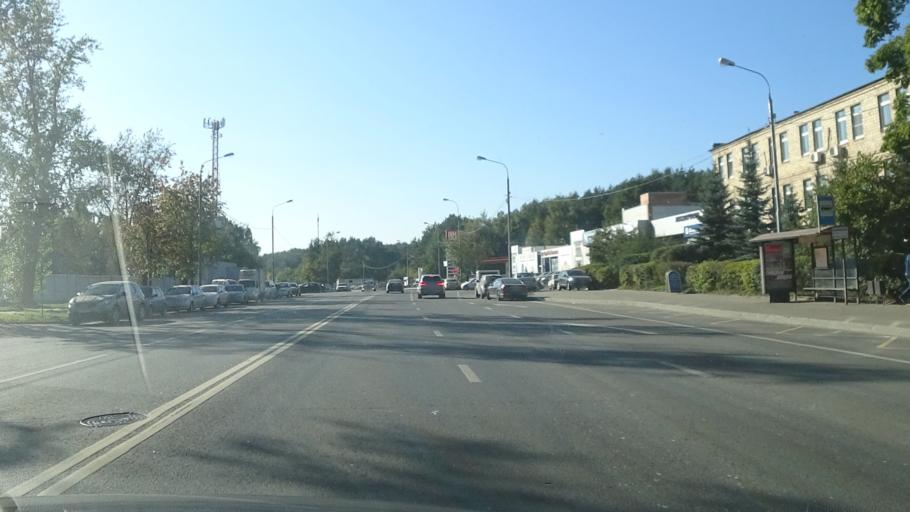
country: RU
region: Moskovskaya
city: Bol'shaya Setun'
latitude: 55.7340
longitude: 37.3939
